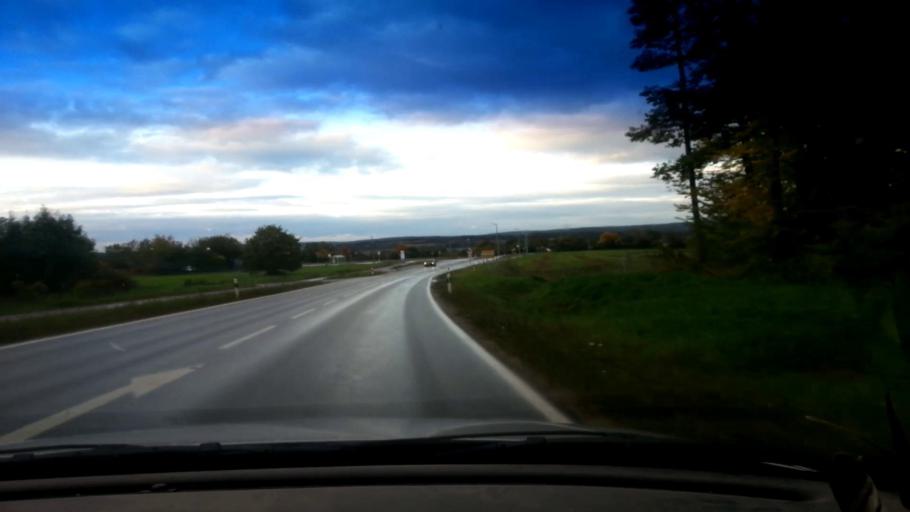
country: DE
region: Bavaria
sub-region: Upper Franconia
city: Burgebrach
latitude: 49.8182
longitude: 10.7339
